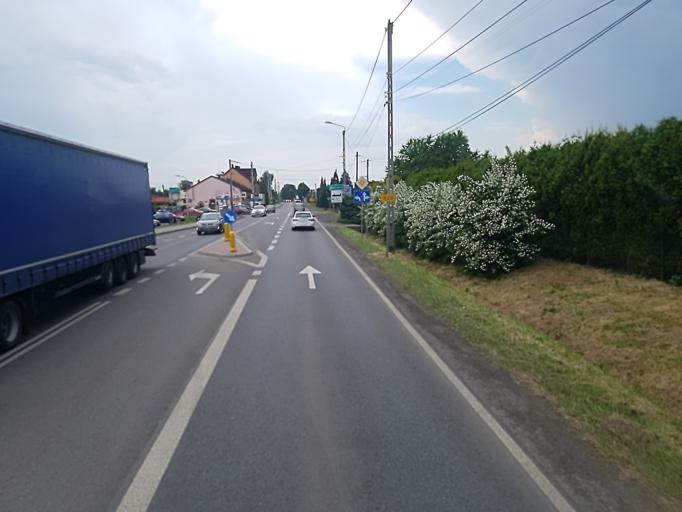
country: PL
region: Silesian Voivodeship
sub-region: Powiat wodzislawski
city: Mszana
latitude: 49.9856
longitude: 18.5064
